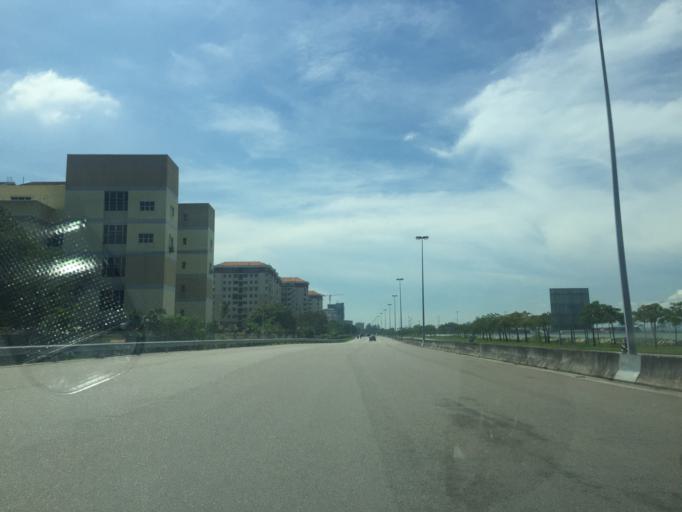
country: MY
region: Penang
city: Butterworth
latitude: 5.4289
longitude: 100.3762
